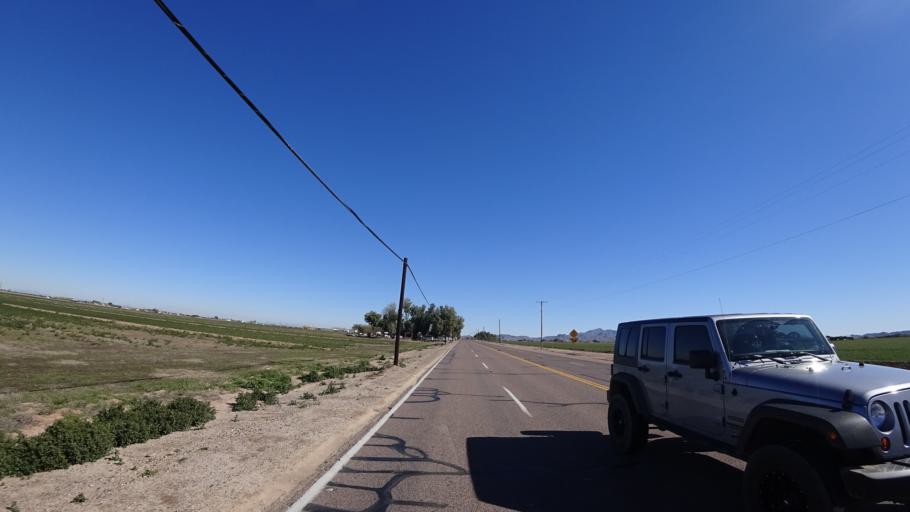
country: US
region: Arizona
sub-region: Maricopa County
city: Buckeye
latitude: 33.3776
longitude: -112.4947
